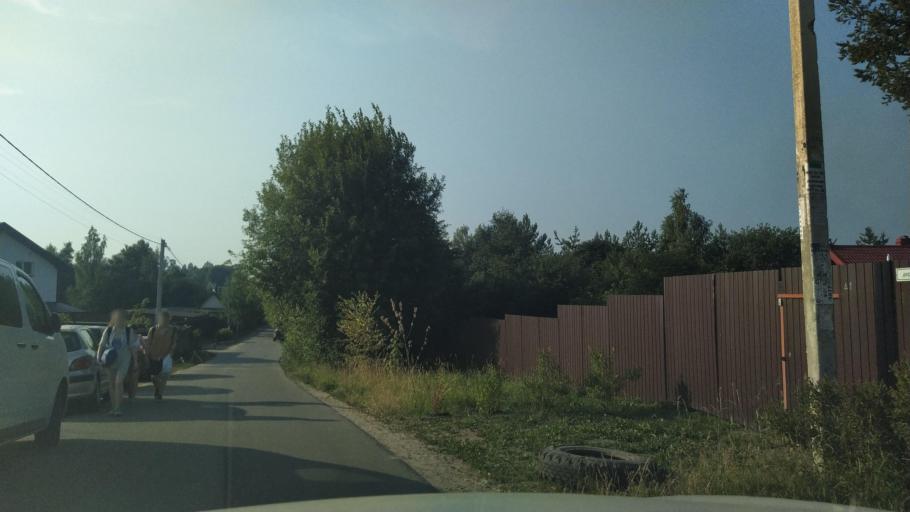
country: RU
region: Leningrad
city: Koltushi
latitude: 59.8909
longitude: 30.7324
